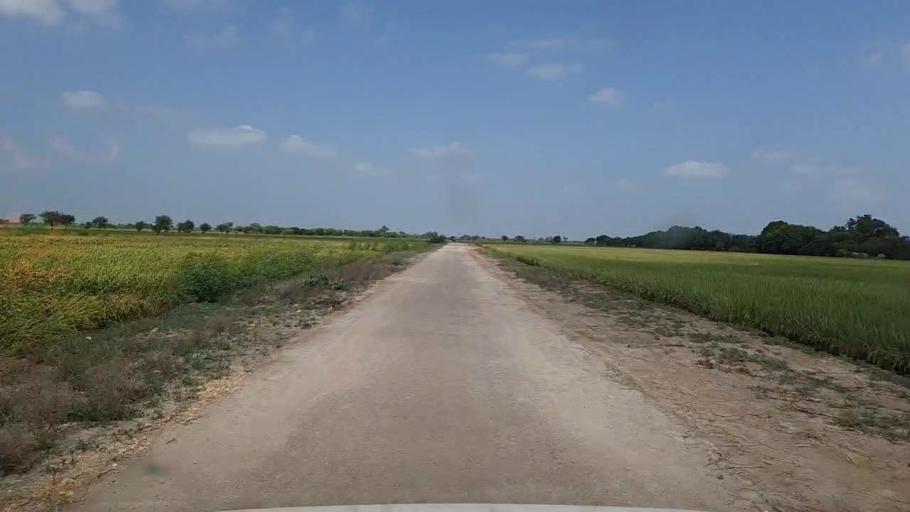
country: PK
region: Sindh
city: Kario
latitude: 24.6856
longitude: 68.5880
